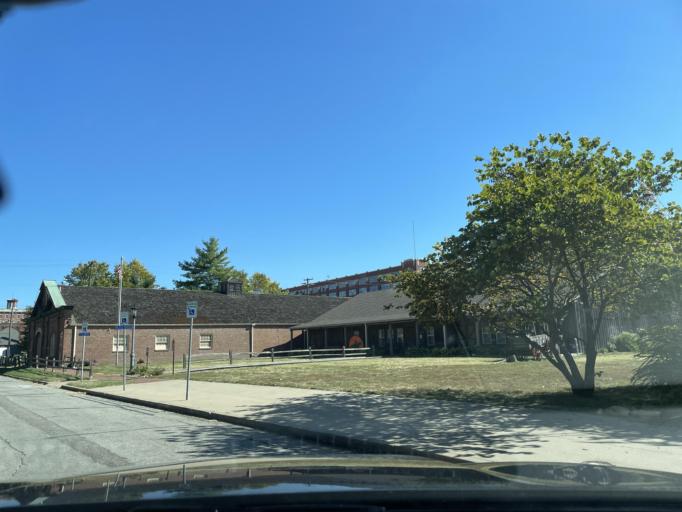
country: US
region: Missouri
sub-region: Buchanan County
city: Saint Joseph
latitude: 39.7563
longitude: -94.8493
